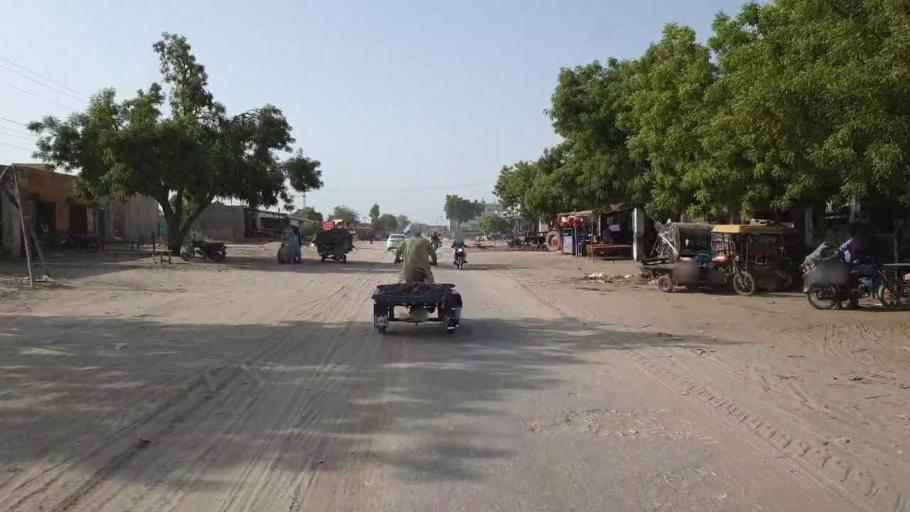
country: PK
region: Sindh
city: Sanghar
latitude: 26.2735
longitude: 68.9300
